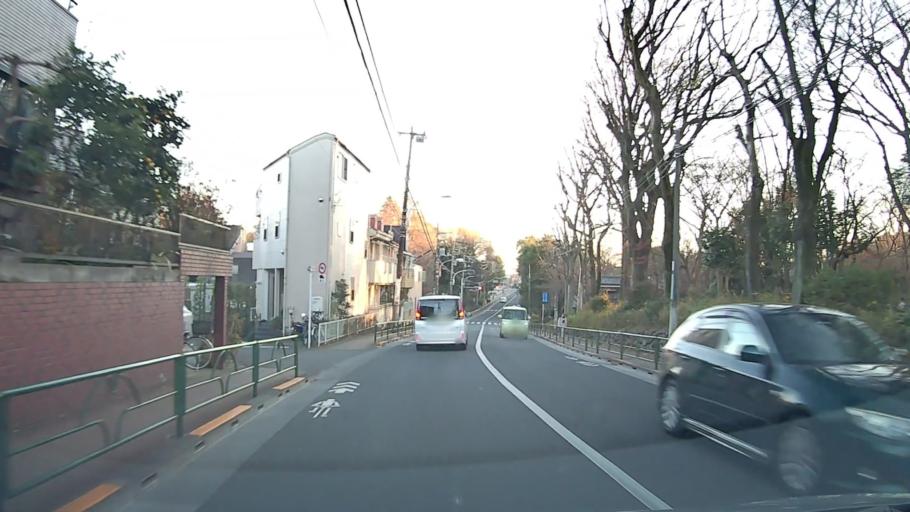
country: JP
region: Tokyo
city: Musashino
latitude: 35.7392
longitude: 139.5980
